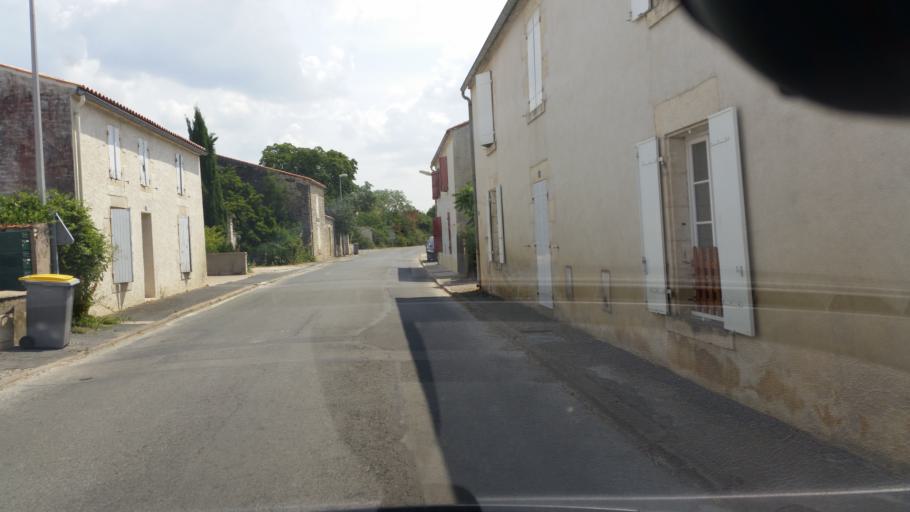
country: FR
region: Poitou-Charentes
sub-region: Departement de la Charente-Maritime
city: Saint-Jean-de-Liversay
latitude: 46.2151
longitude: -0.8841
